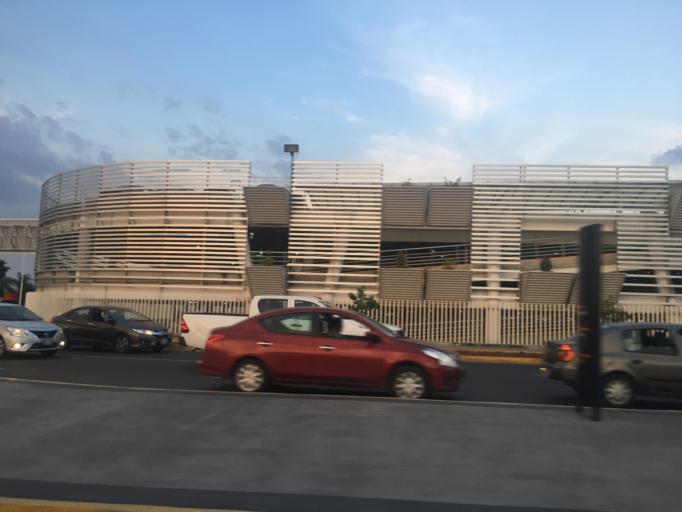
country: MX
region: Jalisco
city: El Quince
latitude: 20.5265
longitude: -103.3023
